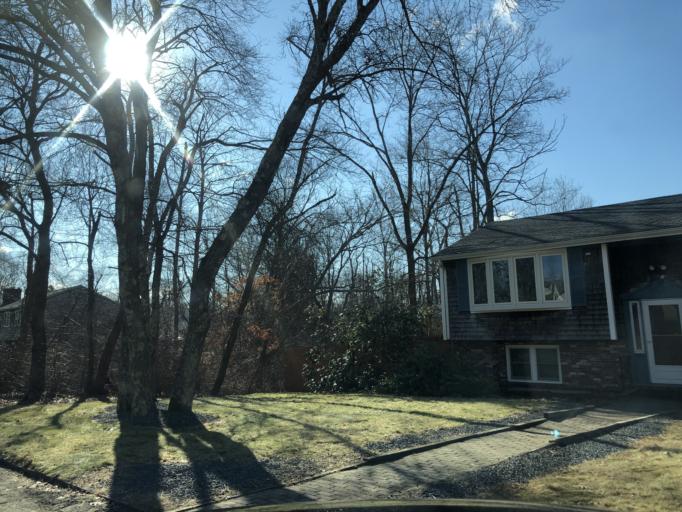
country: US
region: Massachusetts
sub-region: Plymouth County
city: Brockton
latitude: 42.1134
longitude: -71.0143
